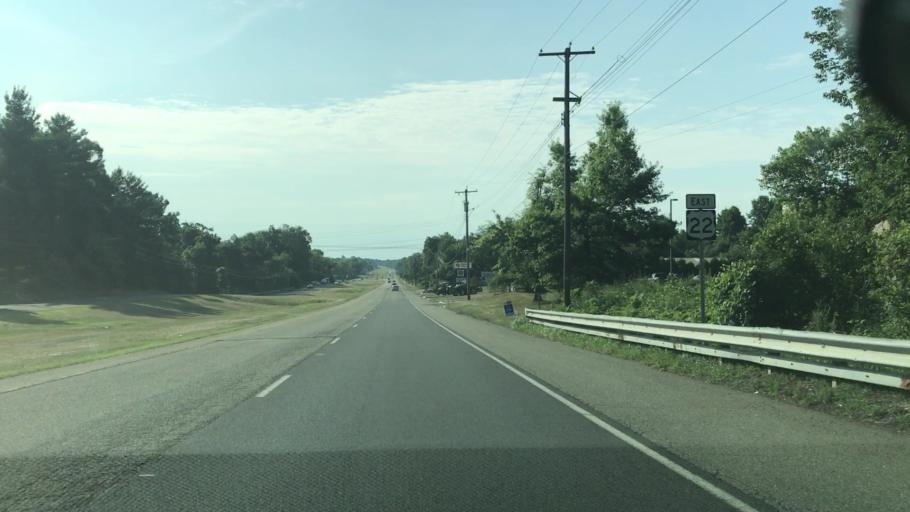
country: US
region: New Jersey
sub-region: Hunterdon County
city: Whitehouse Station
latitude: 40.6370
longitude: -74.7903
